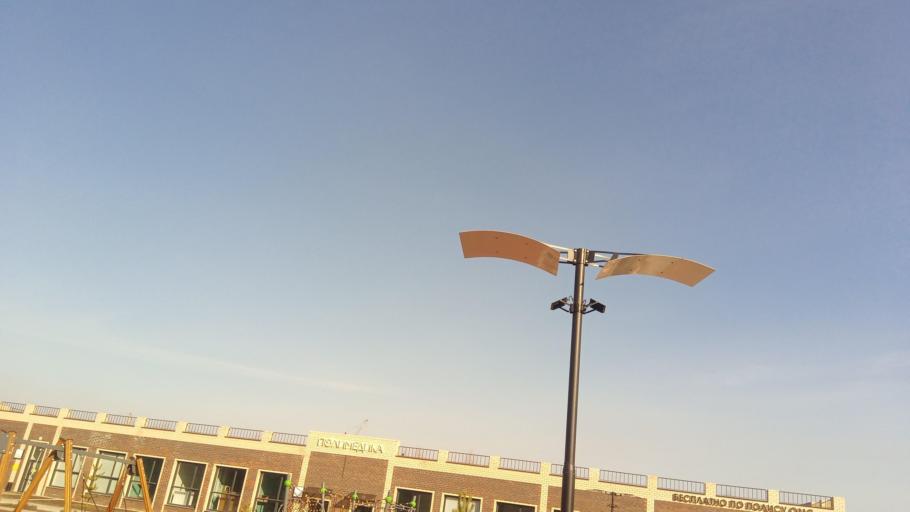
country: RU
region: Chelyabinsk
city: Sargazy
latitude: 55.1127
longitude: 61.2513
